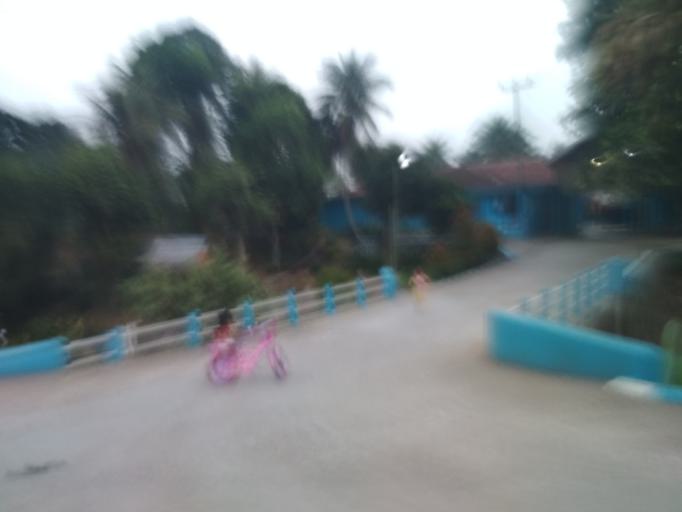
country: ID
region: West Java
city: Caringin
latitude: -6.7032
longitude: 106.8257
